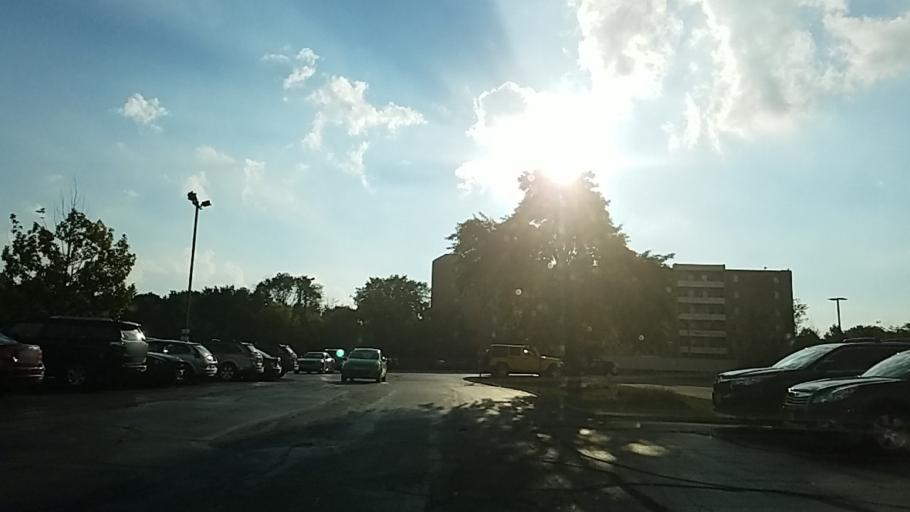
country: US
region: Ohio
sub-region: Cuyahoga County
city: Shaker Heights
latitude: 41.4610
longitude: -81.5351
